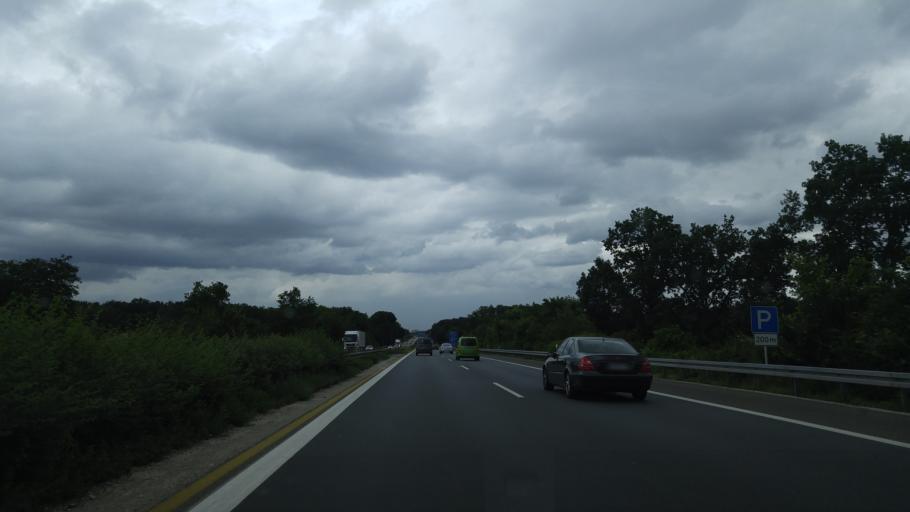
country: DE
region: Bavaria
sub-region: Regierungsbezirk Mittelfranken
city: Furth
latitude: 49.5288
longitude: 10.9925
